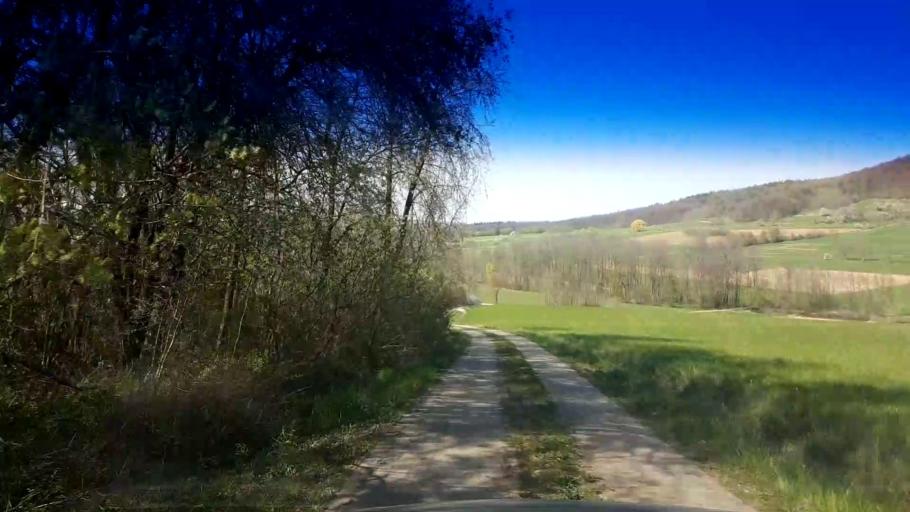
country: DE
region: Bavaria
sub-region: Upper Franconia
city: Schesslitz
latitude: 49.9437
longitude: 11.0452
